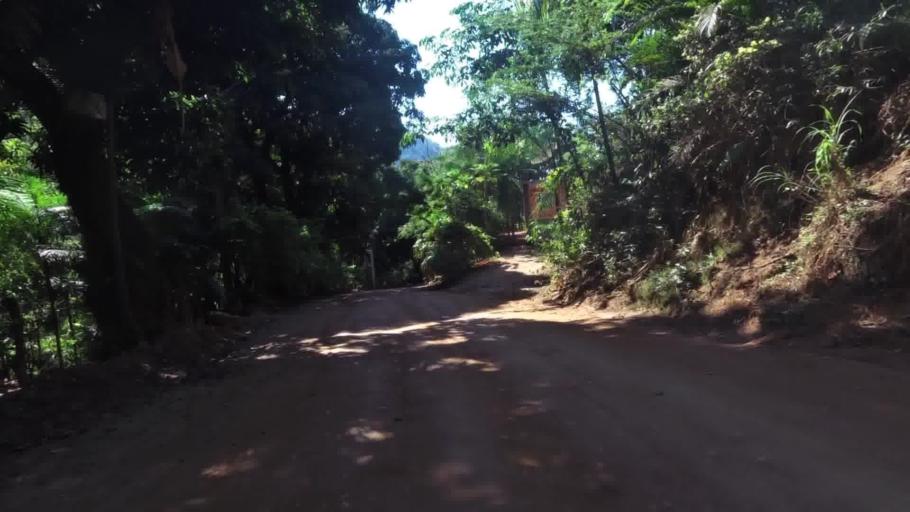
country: BR
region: Espirito Santo
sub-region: Alfredo Chaves
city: Alfredo Chaves
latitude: -20.6456
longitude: -40.7952
